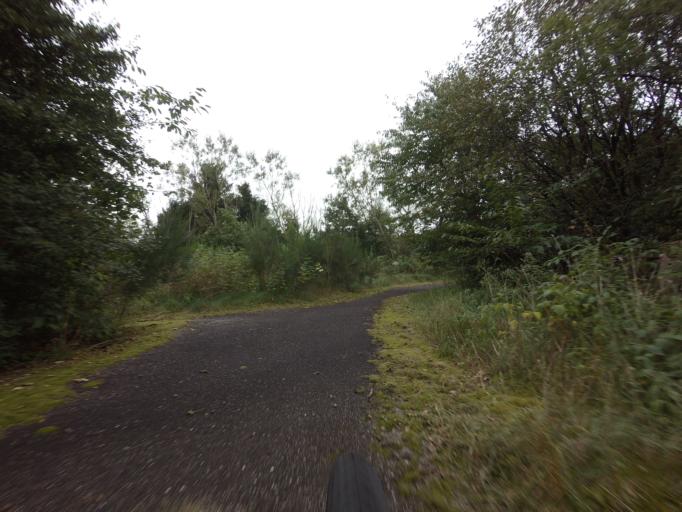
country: DK
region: Central Jutland
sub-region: Ikast-Brande Kommune
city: Brande
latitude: 55.9200
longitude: 9.1187
